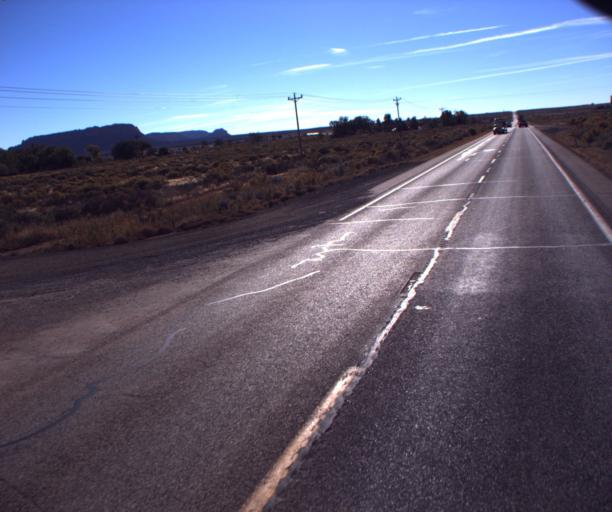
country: US
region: Arizona
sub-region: Mohave County
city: Colorado City
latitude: 36.9323
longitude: -112.9447
